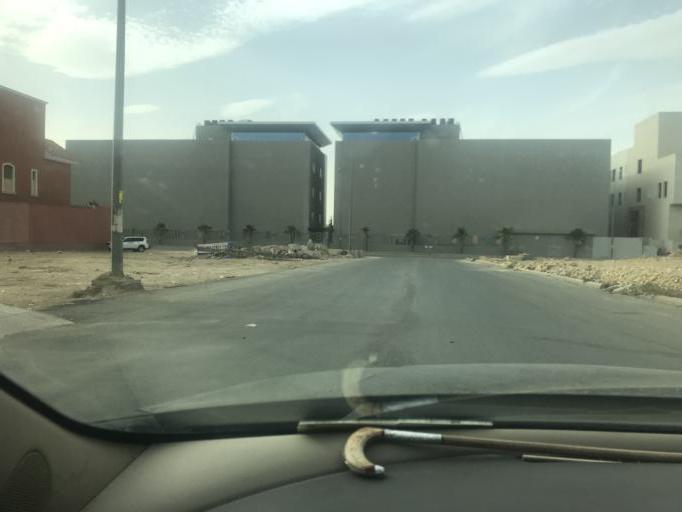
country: SA
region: Ar Riyad
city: Riyadh
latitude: 24.8075
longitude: 46.6677
